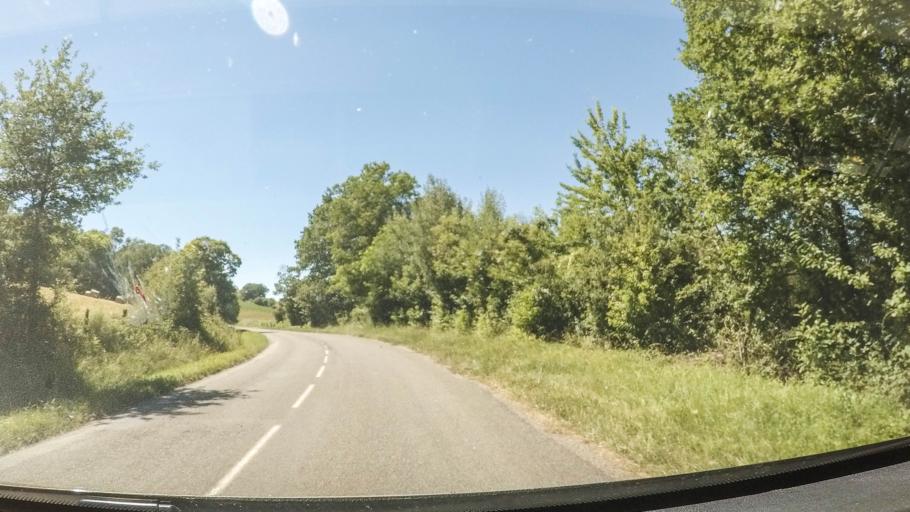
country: FR
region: Midi-Pyrenees
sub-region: Departement de l'Aveyron
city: Saint-Christophe-Vallon
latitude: 44.4689
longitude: 2.3705
